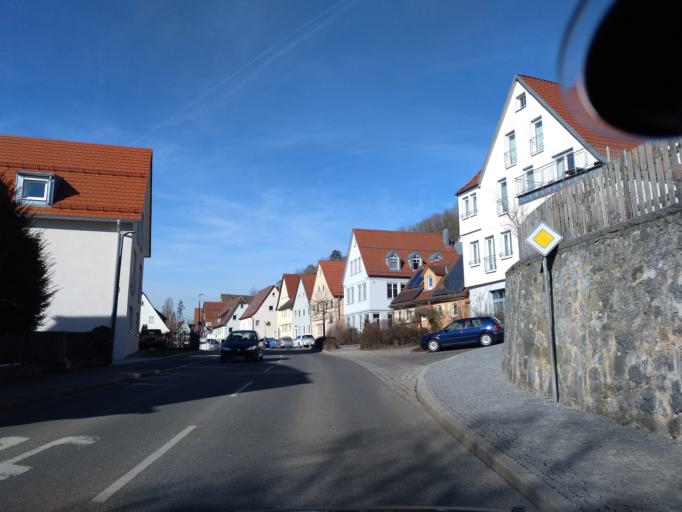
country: DE
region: Baden-Wuerttemberg
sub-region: Regierungsbezirk Stuttgart
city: Schwaebisch Hall
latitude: 49.1071
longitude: 9.7414
